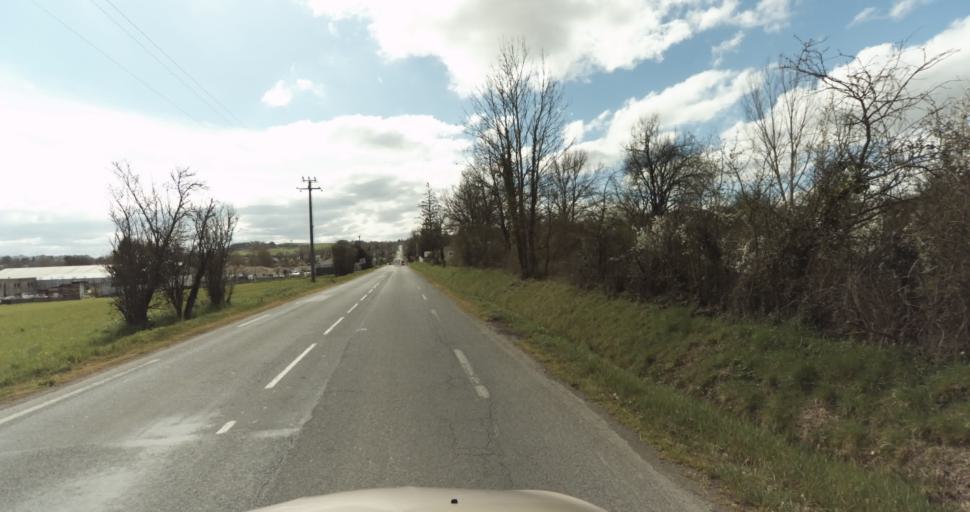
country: FR
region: Midi-Pyrenees
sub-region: Departement du Tarn
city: Puygouzon
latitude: 43.8950
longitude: 2.1515
